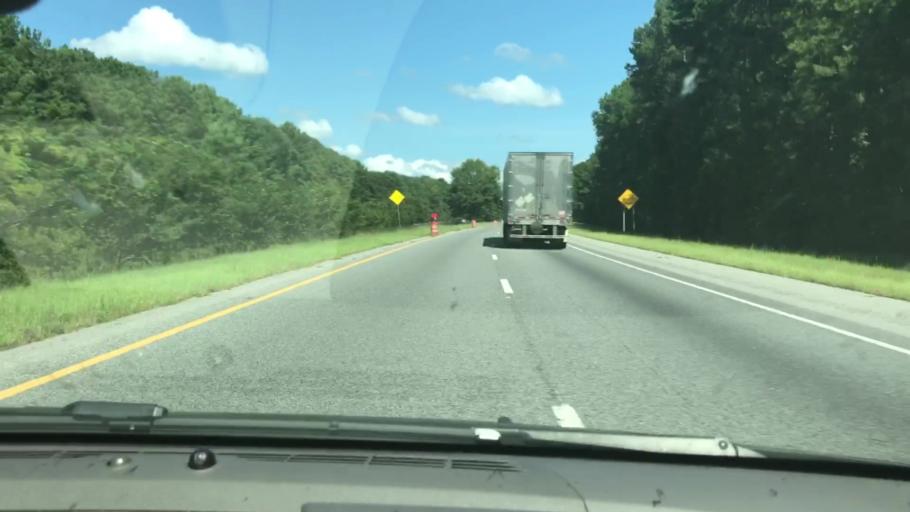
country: US
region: Georgia
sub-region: Harris County
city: Hamilton
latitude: 32.7044
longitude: -85.0092
